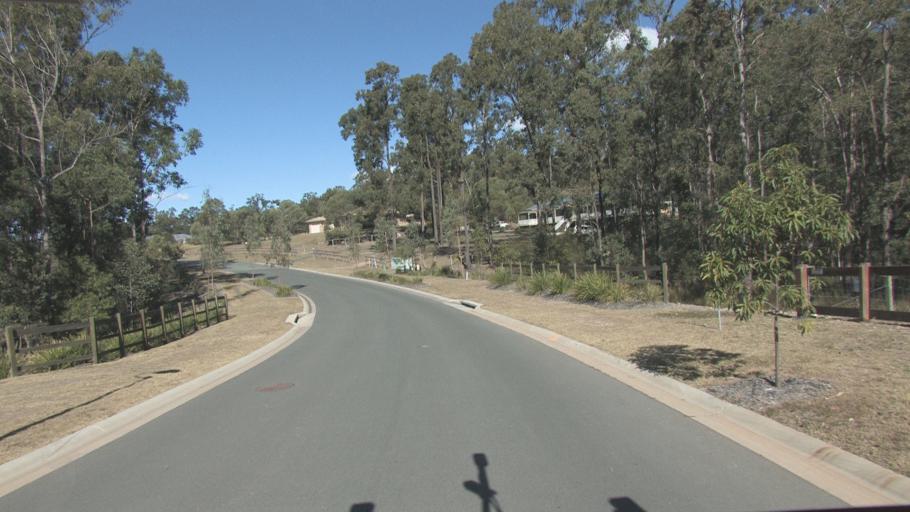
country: AU
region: Queensland
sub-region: Ipswich
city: Springfield Lakes
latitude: -27.7336
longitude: 152.9064
